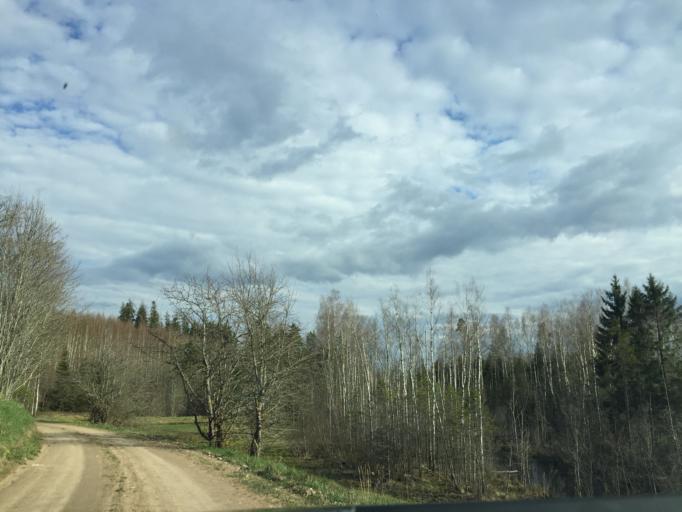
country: LV
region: Aluksnes Rajons
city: Aluksne
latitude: 57.4032
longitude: 26.9768
